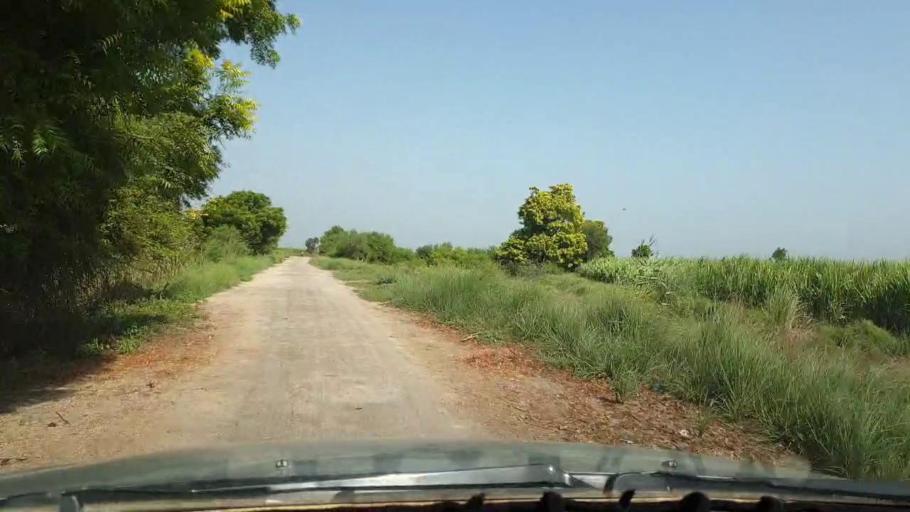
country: PK
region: Sindh
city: Matli
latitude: 25.0938
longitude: 68.6097
